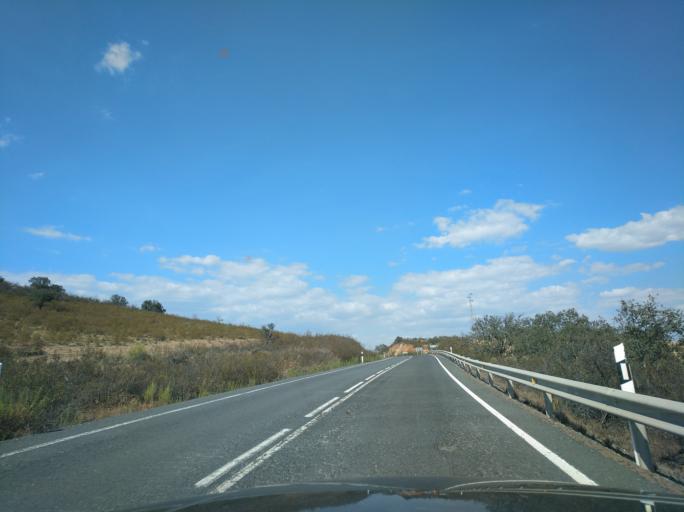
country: ES
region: Andalusia
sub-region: Provincia de Huelva
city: Cabezas Rubias
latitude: 37.6770
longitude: -7.1098
